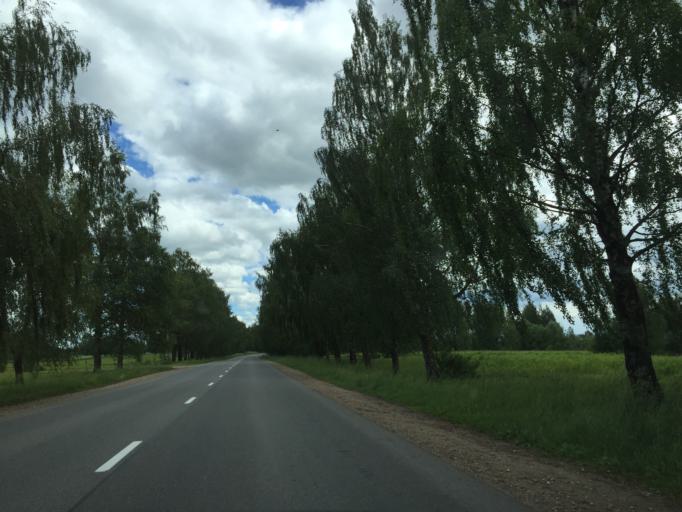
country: LV
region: Lecava
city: Iecava
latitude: 56.6046
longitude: 24.2107
